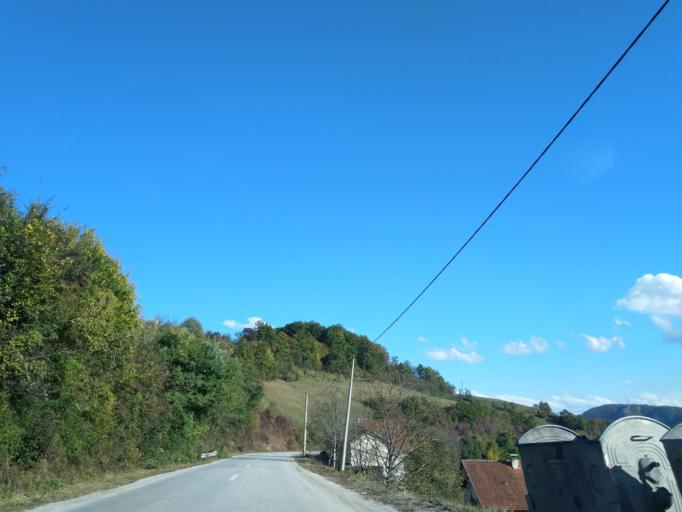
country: RS
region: Central Serbia
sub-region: Zlatiborski Okrug
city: Uzice
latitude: 43.8696
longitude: 19.7990
